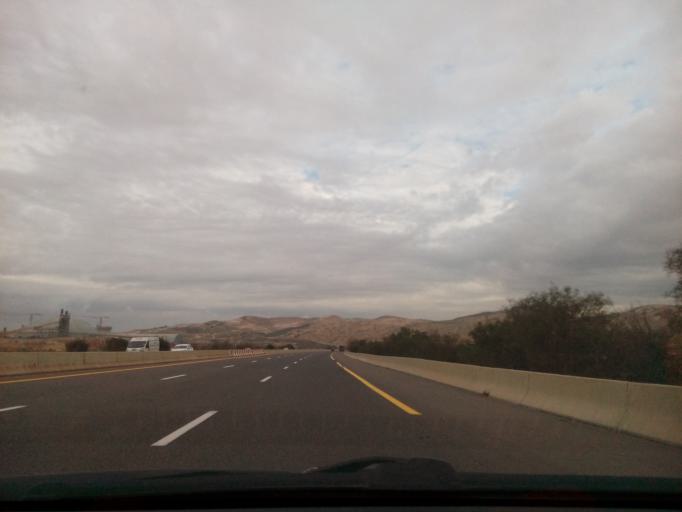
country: DZ
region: Sidi Bel Abbes
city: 'Ain el Berd
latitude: 35.4500
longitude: -0.3966
